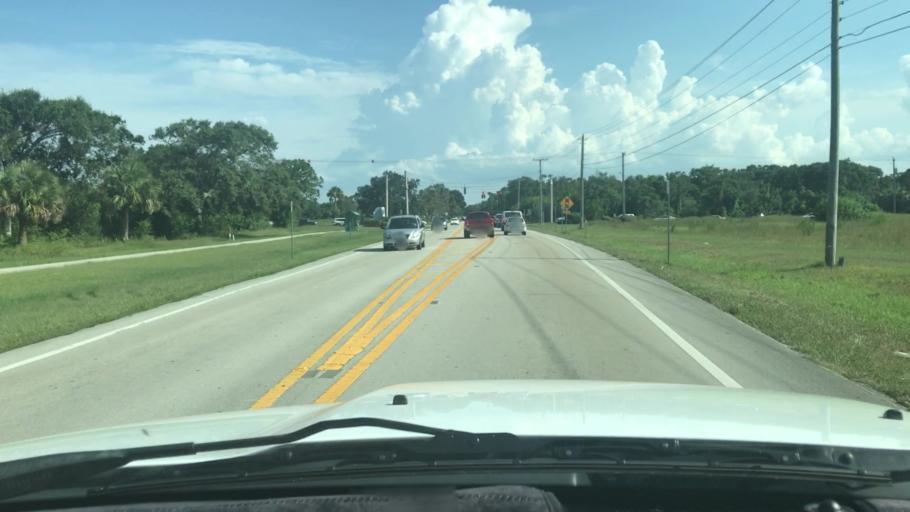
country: US
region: Florida
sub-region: Indian River County
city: Vero Beach
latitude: 27.6475
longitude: -80.4301
